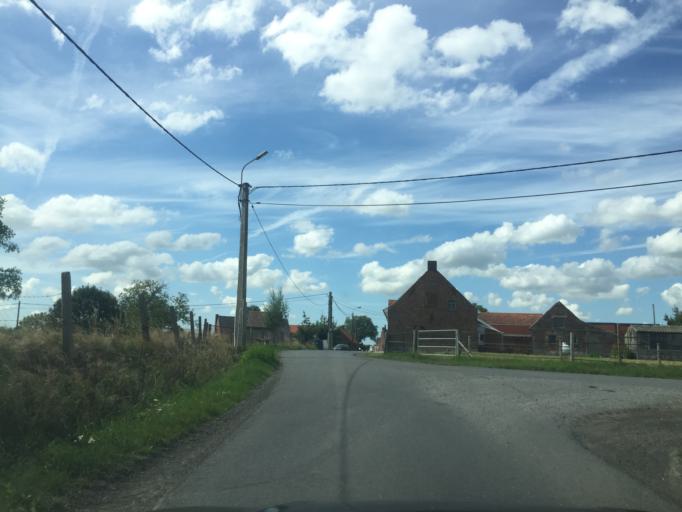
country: BE
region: Flanders
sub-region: Provincie West-Vlaanderen
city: Staden
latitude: 50.9609
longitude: 2.9999
